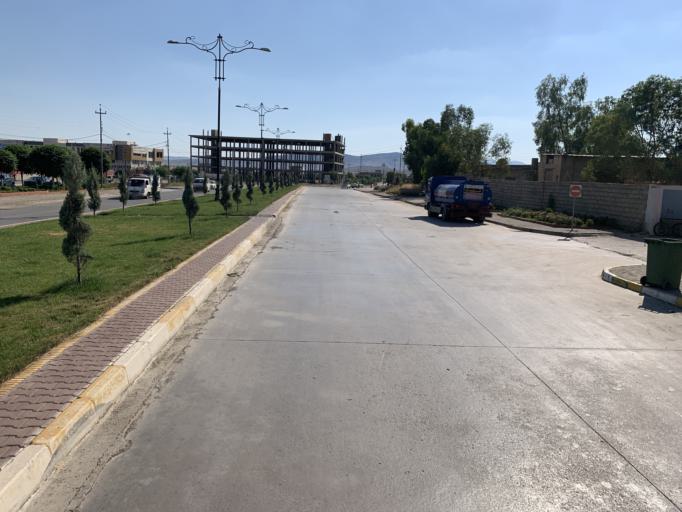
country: IQ
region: As Sulaymaniyah
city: Raniye
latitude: 36.2327
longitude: 44.7877
